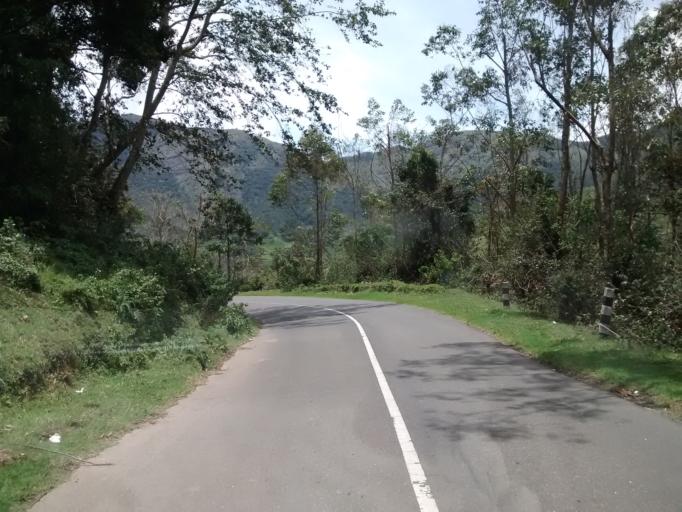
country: IN
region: Kerala
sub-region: Idukki
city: Munnar
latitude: 10.1328
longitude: 77.2048
